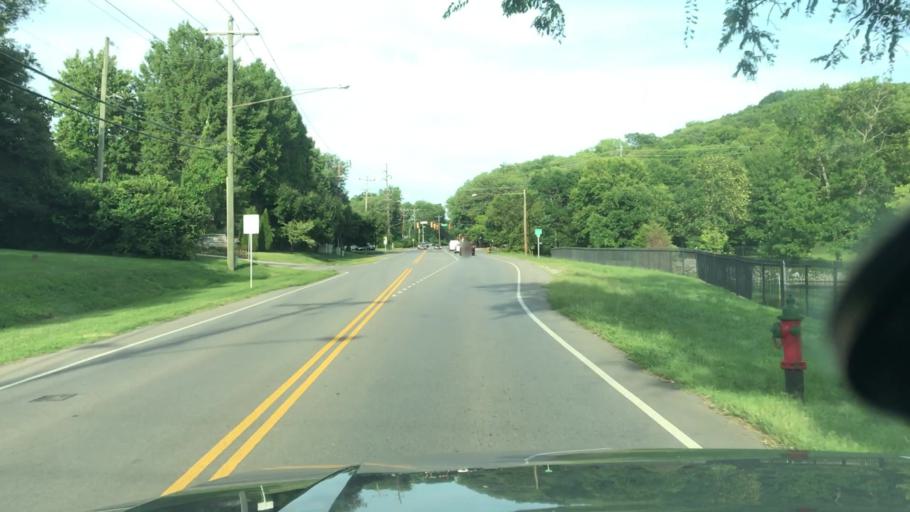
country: US
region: Tennessee
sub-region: Davidson County
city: Belle Meade
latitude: 36.0914
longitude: -86.8307
